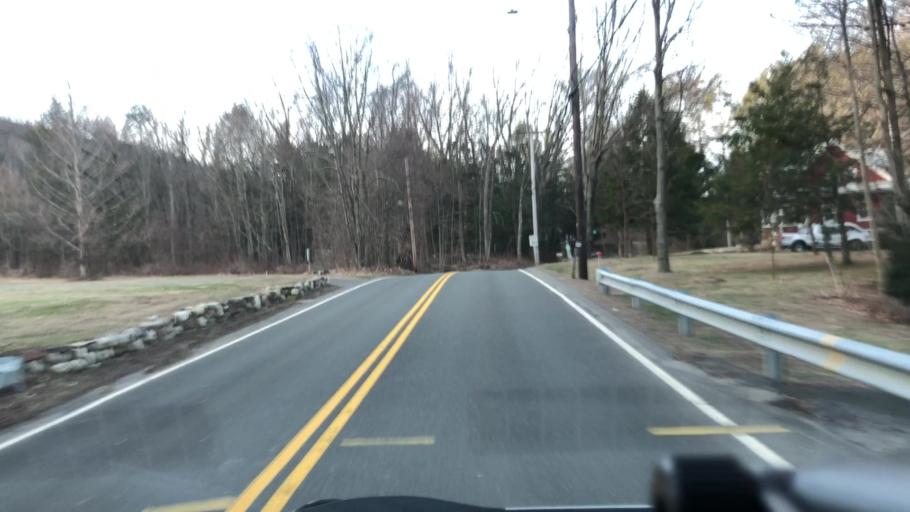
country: US
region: Massachusetts
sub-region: Hampshire County
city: Easthampton
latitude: 42.2487
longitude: -72.6537
